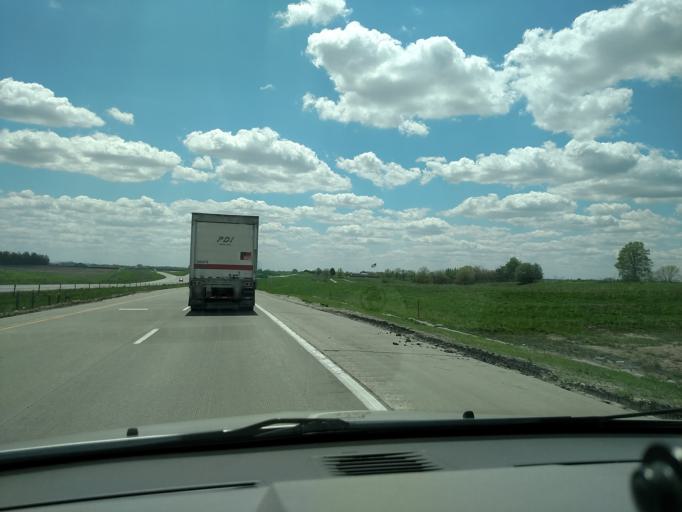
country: US
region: Iowa
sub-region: Polk County
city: Ankeny
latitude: 41.7695
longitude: -93.5706
